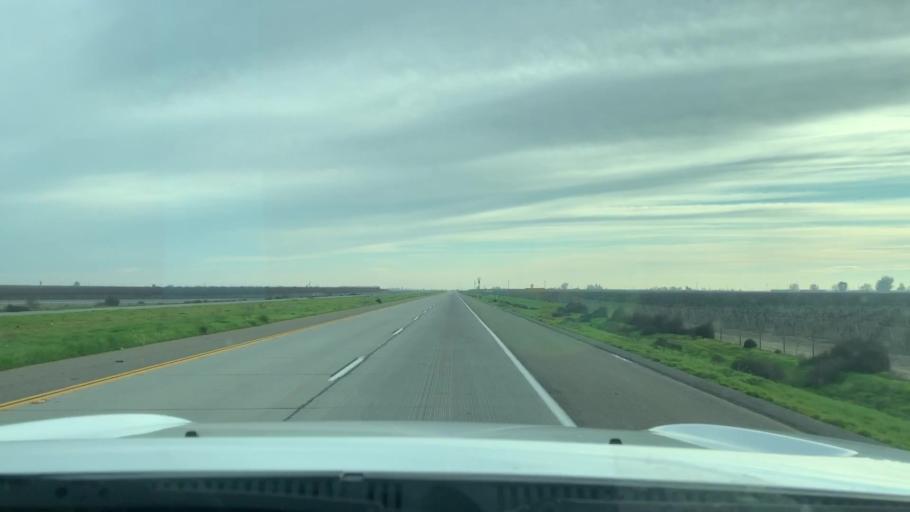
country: US
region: California
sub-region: Fresno County
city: Easton
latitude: 36.5898
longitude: -119.7862
